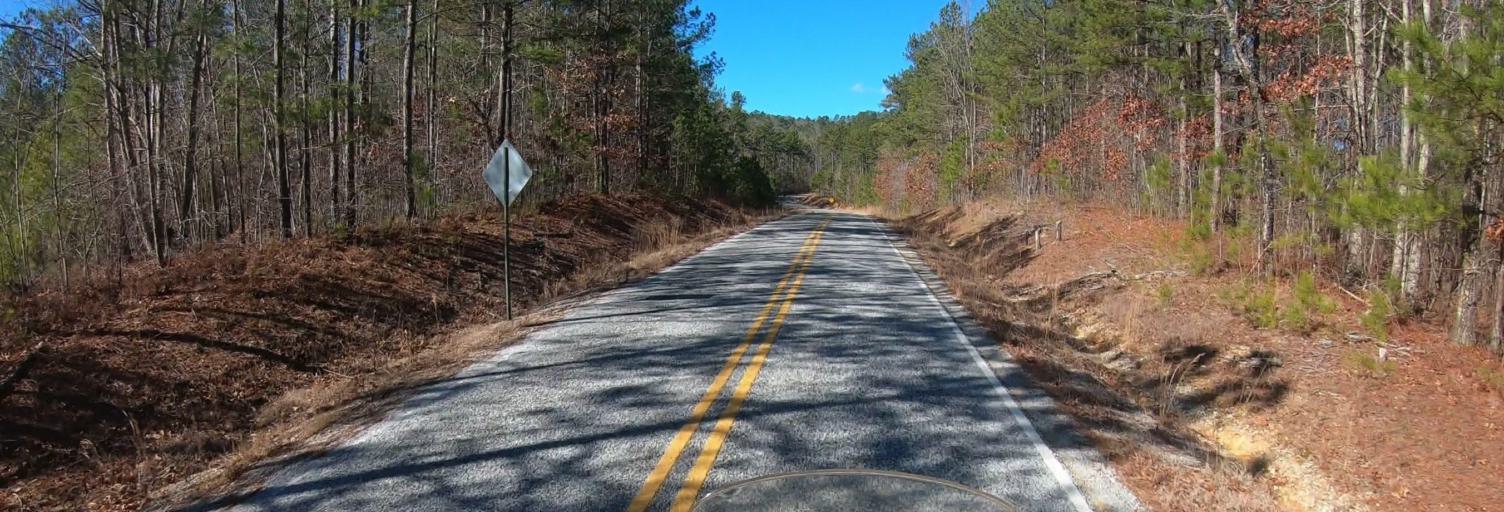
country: US
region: Alabama
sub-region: Clay County
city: Ashland
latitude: 33.3964
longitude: -85.8693
